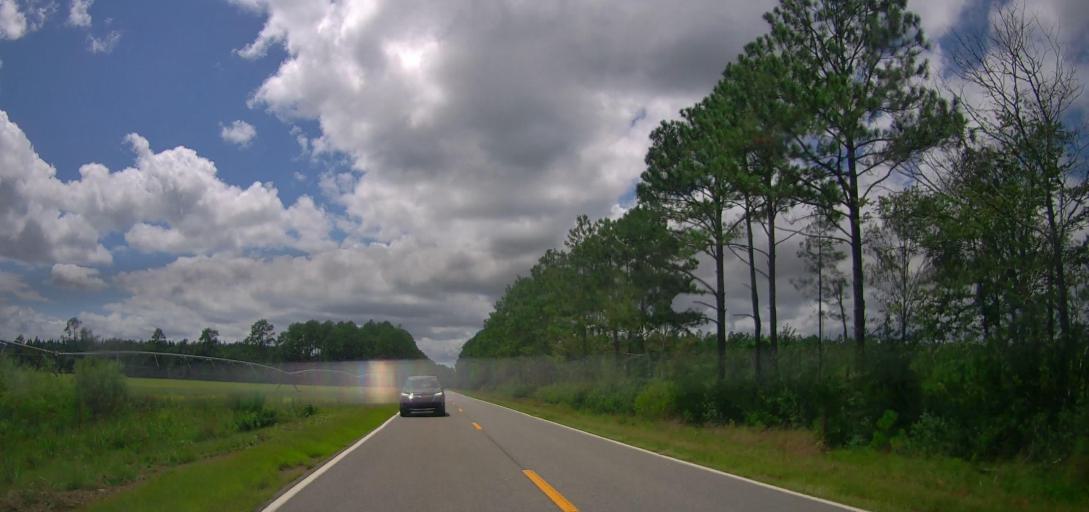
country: US
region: Georgia
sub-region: Irwin County
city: Ocilla
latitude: 31.6460
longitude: -83.3094
